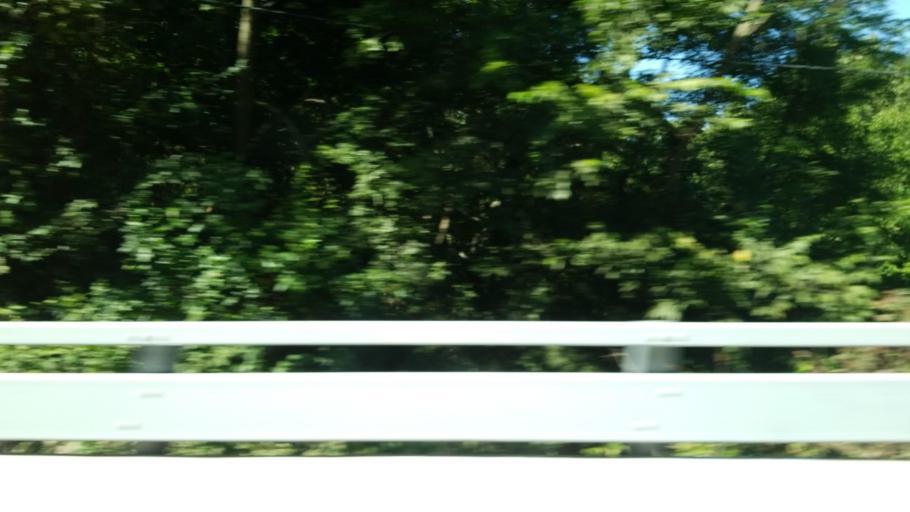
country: US
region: Illinois
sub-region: Saline County
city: Carrier Mills
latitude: 37.8014
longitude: -88.7210
